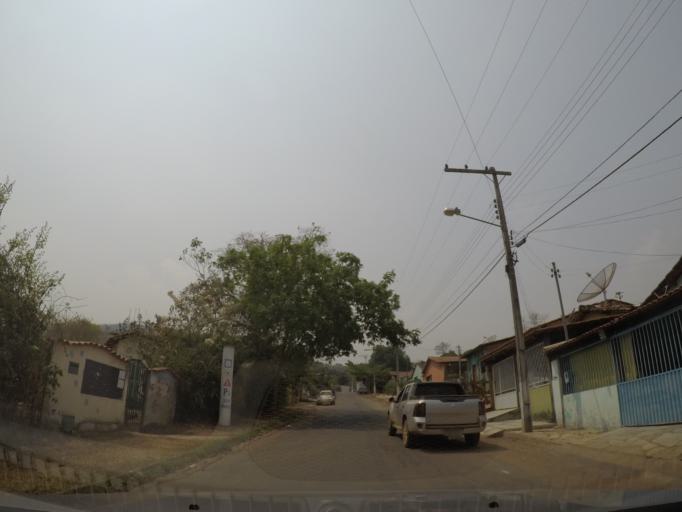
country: BR
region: Goias
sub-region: Pirenopolis
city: Pirenopolis
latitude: -15.8439
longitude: -48.9596
